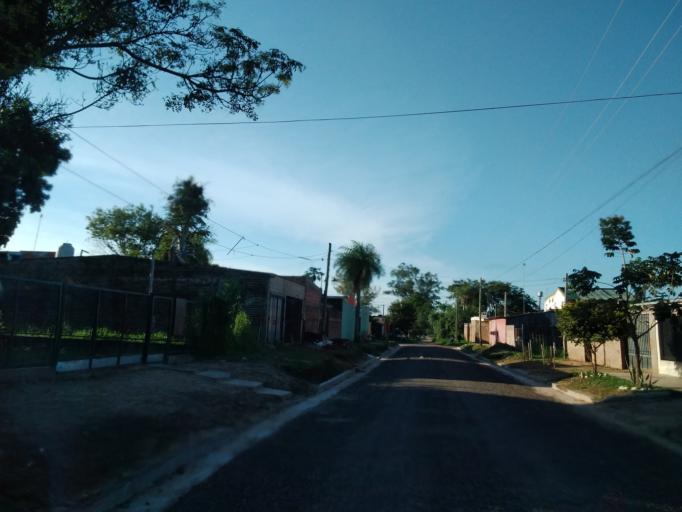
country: AR
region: Corrientes
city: Corrientes
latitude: -27.5054
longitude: -58.7991
